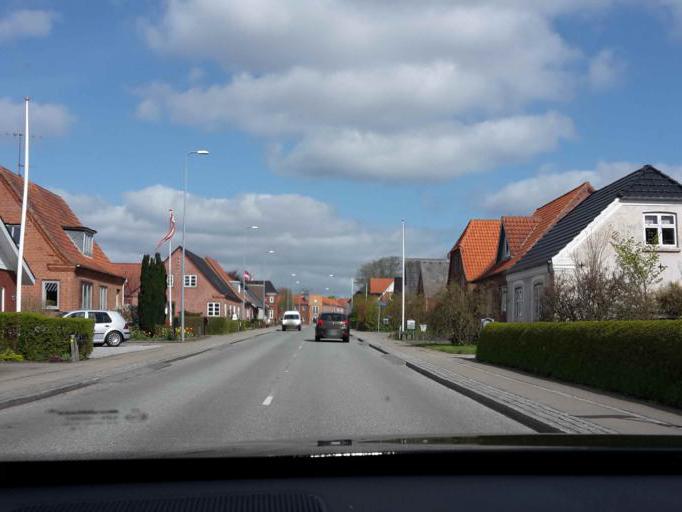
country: DK
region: South Denmark
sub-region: Varde Kommune
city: Olgod
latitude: 55.7358
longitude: 8.7096
